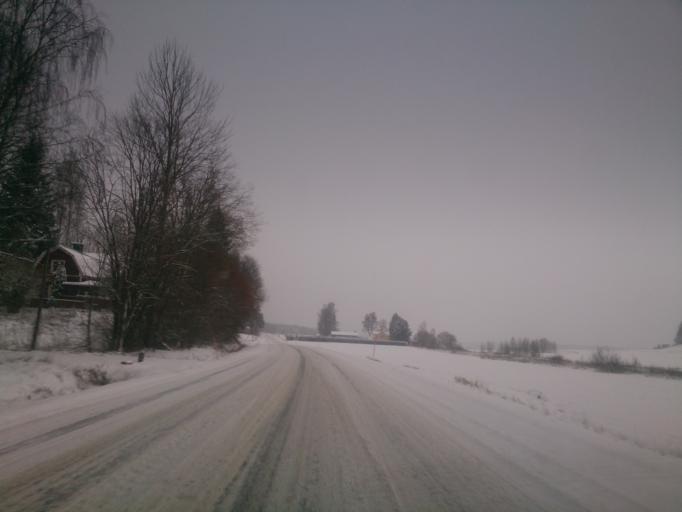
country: SE
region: OEstergoetland
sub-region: Finspangs Kommun
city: Finspang
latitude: 58.6456
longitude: 15.8206
